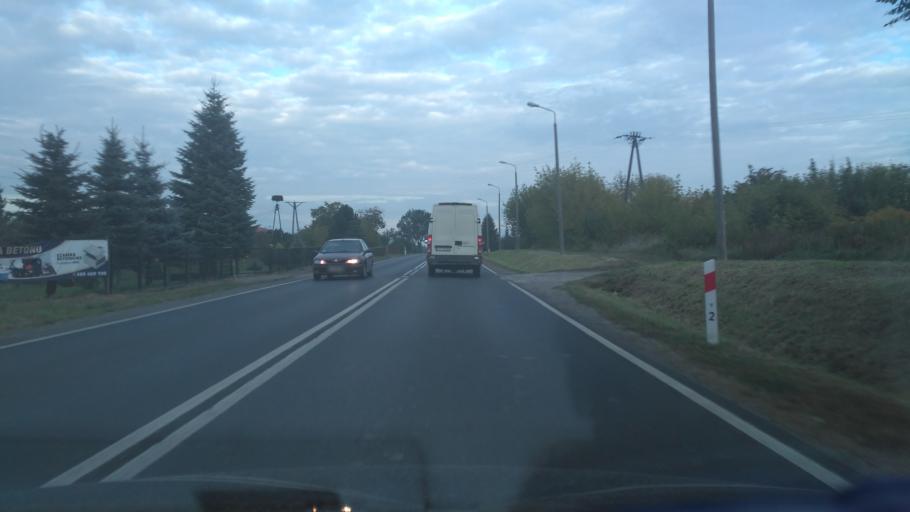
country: PL
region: Lublin Voivodeship
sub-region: Powiat lubelski
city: Jakubowice Murowane
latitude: 51.2874
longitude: 22.6830
